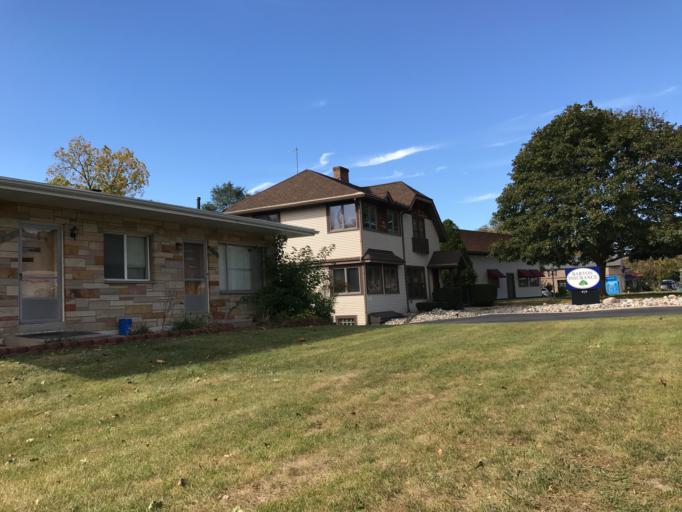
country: US
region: Michigan
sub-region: Washtenaw County
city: Ann Arbor
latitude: 42.2569
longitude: -83.7273
